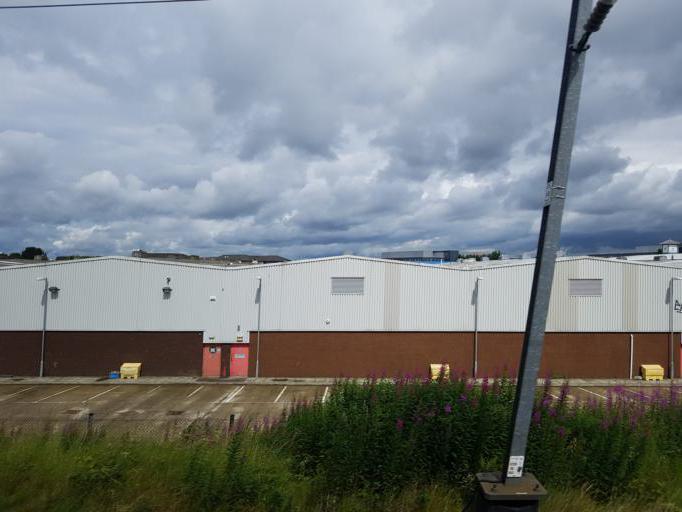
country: GB
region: Scotland
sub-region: Edinburgh
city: Currie
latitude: 55.9289
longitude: -3.2961
